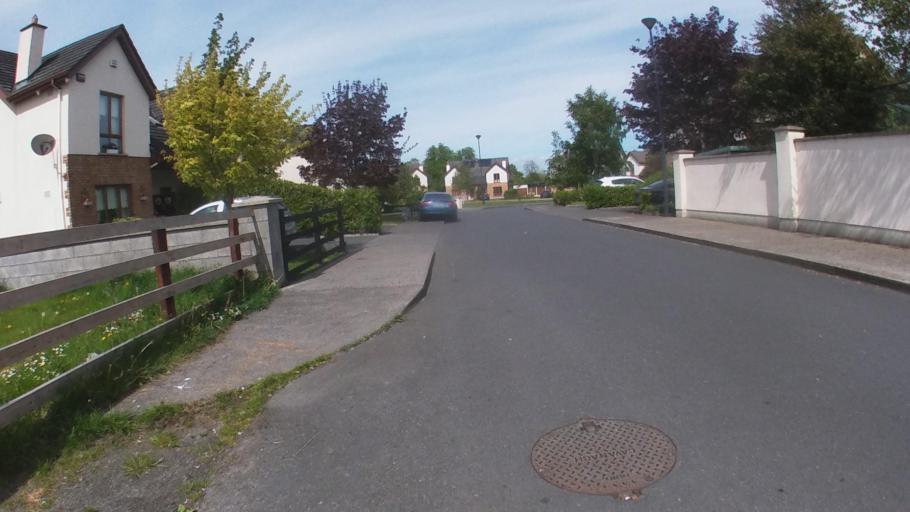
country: IE
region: Leinster
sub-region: County Carlow
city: Carlow
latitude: 52.8493
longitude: -6.9924
